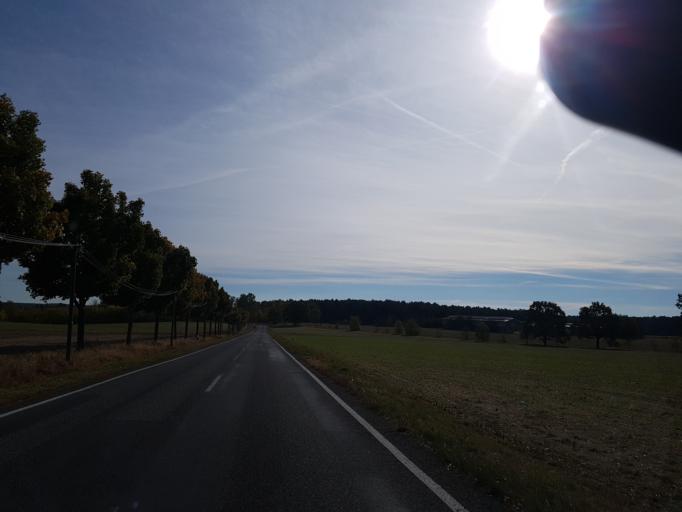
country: DE
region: Brandenburg
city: Ihlow
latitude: 51.8092
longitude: 13.2947
